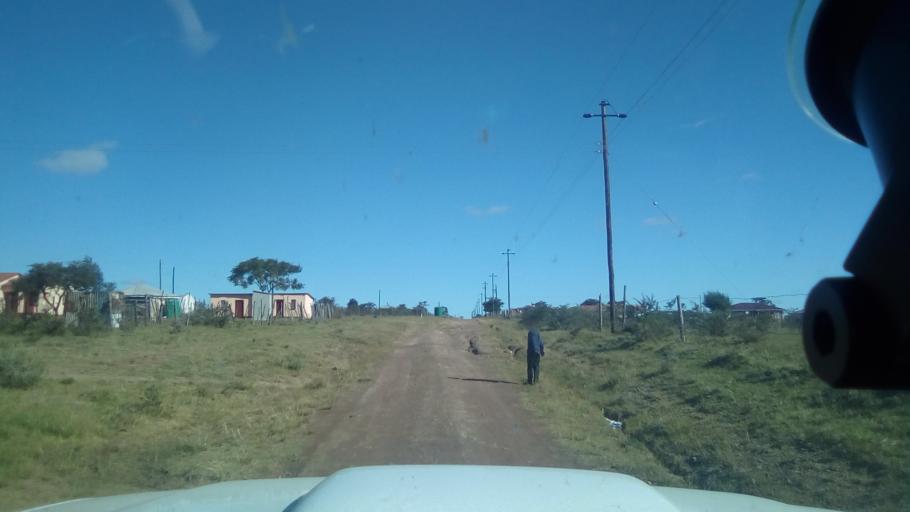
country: ZA
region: Eastern Cape
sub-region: Buffalo City Metropolitan Municipality
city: Bhisho
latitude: -32.7823
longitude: 27.3354
